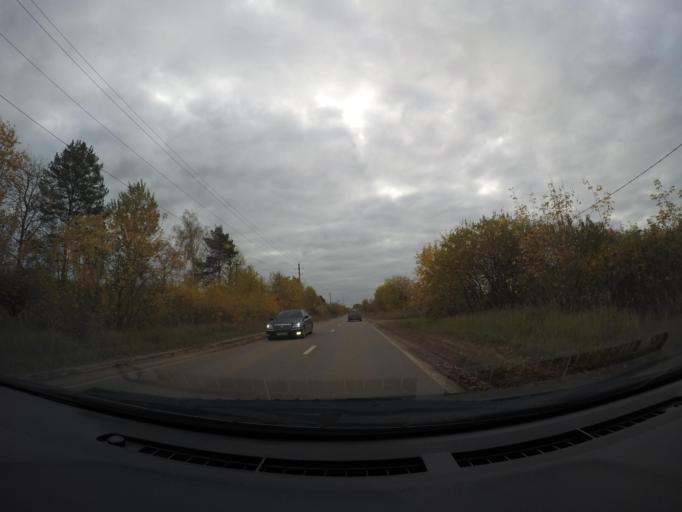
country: RU
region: Moskovskaya
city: Rechitsy
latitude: 55.6197
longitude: 38.4398
